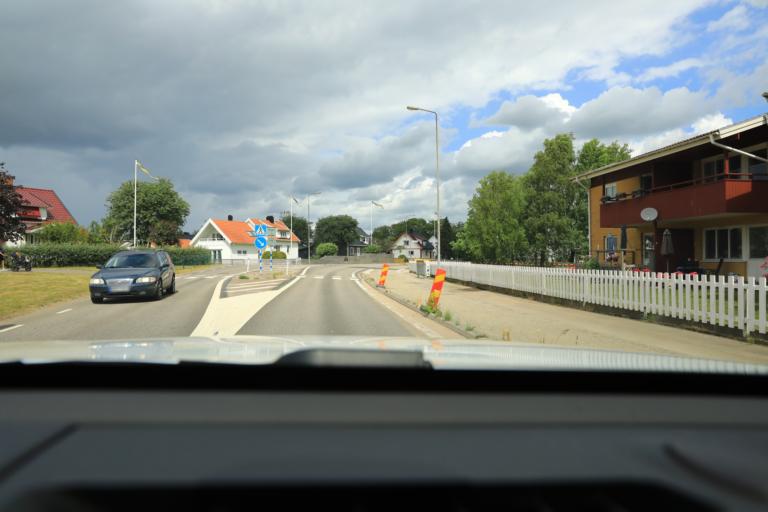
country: SE
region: Halland
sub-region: Varbergs Kommun
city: Tvaaker
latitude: 57.0392
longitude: 12.3990
